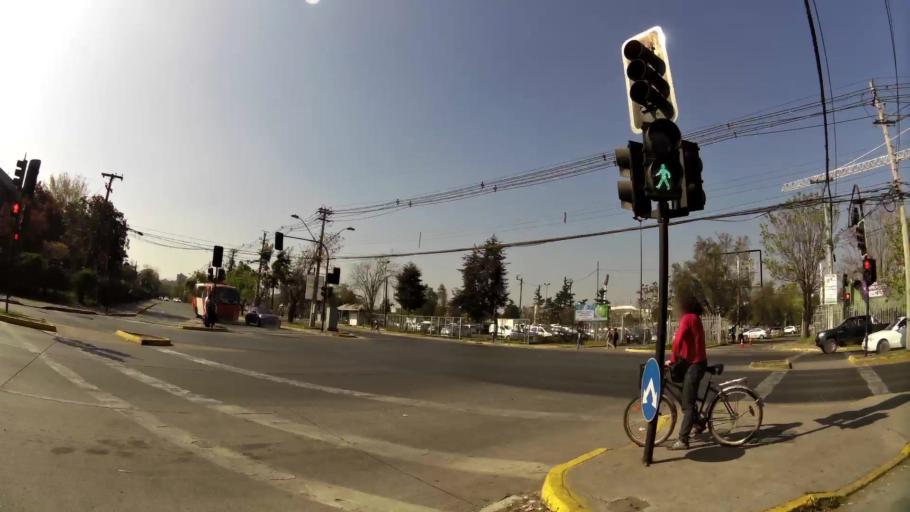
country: CL
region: Santiago Metropolitan
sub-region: Provincia de Santiago
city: Santiago
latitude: -33.4658
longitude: -70.6150
